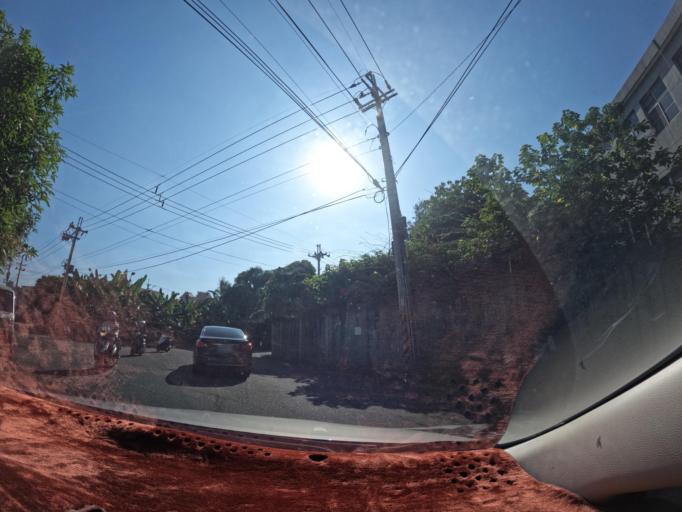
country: TW
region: Taiwan
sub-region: Tainan
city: Tainan
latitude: 23.0231
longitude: 120.2456
